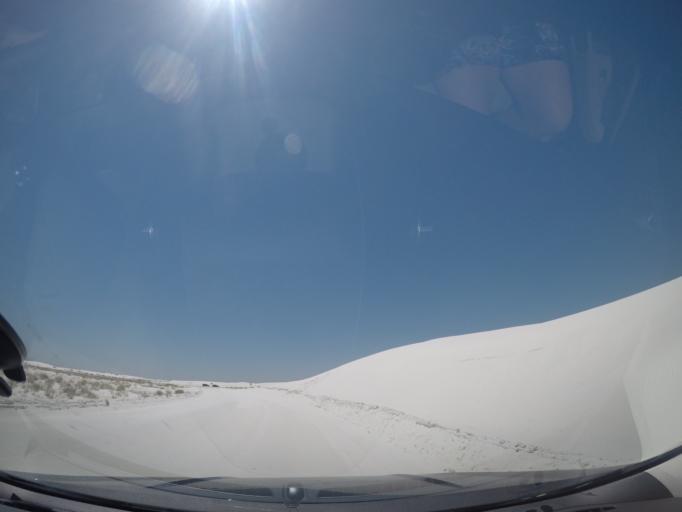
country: US
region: New Mexico
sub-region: Otero County
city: Holloman Air Force Base
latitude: 32.8080
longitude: -106.2622
